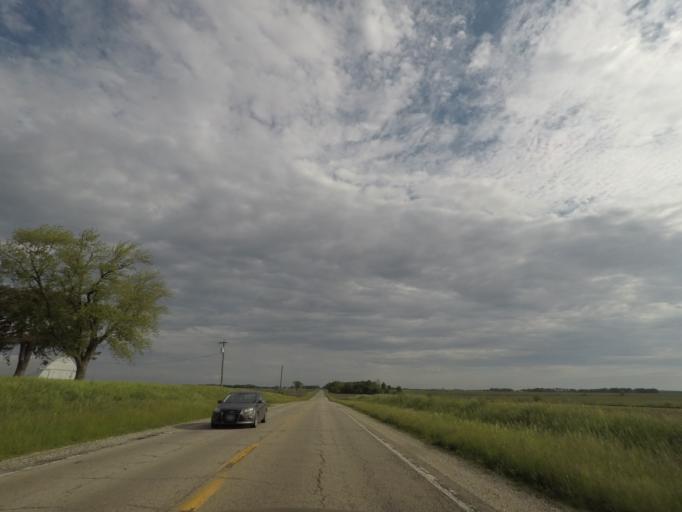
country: US
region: Illinois
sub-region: Logan County
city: Mount Pulaski
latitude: 40.0293
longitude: -89.2822
